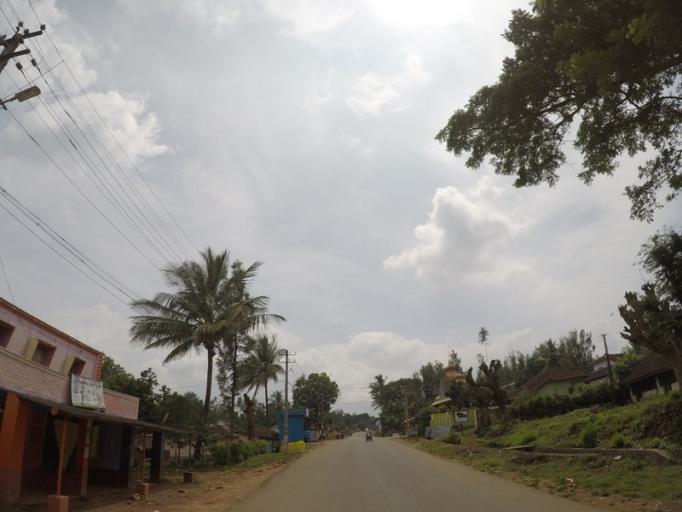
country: IN
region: Karnataka
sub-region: Chikmagalur
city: Chikmagalur
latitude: 13.4185
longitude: 75.8010
